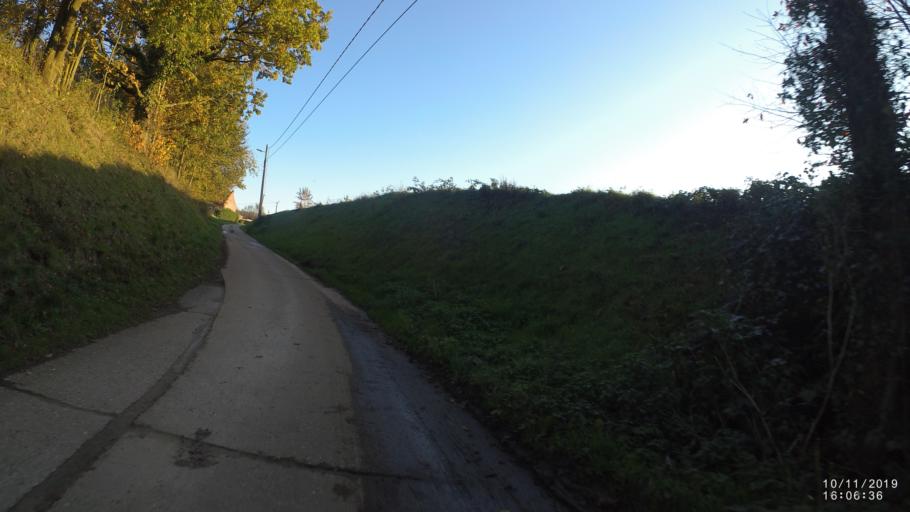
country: BE
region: Flanders
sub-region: Provincie Vlaams-Brabant
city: Lubbeek
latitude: 50.8997
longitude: 4.8545
